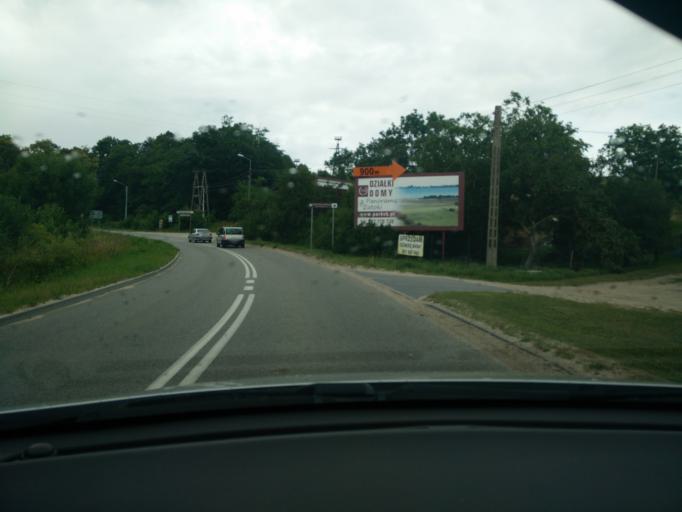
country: PL
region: Pomeranian Voivodeship
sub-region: Powiat pucki
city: Mrzezino
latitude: 54.6482
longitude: 18.4350
